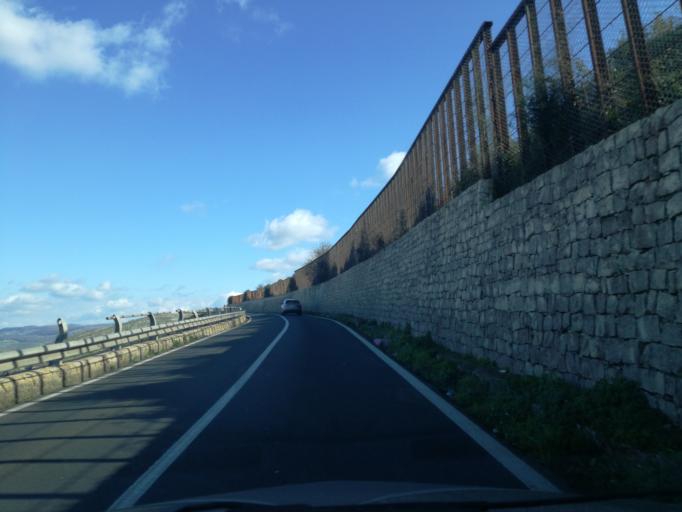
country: IT
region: Sicily
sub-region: Ragusa
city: Comiso
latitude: 36.9389
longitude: 14.6288
